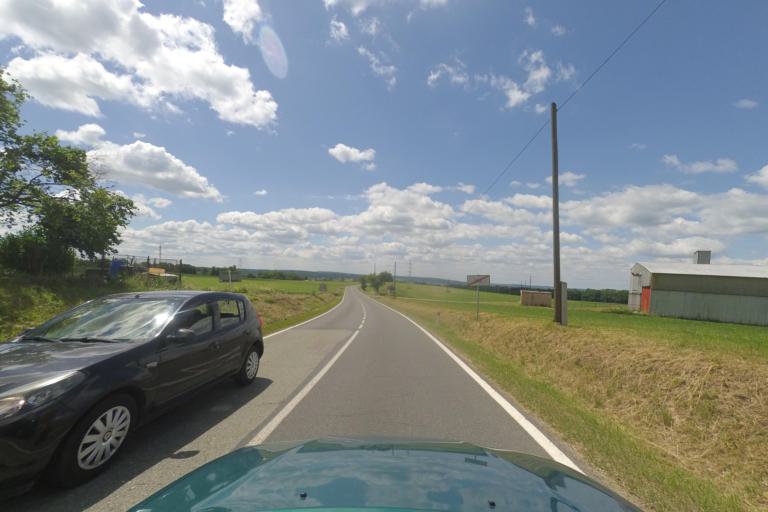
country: CZ
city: Dobruska
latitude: 50.3075
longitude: 16.1842
